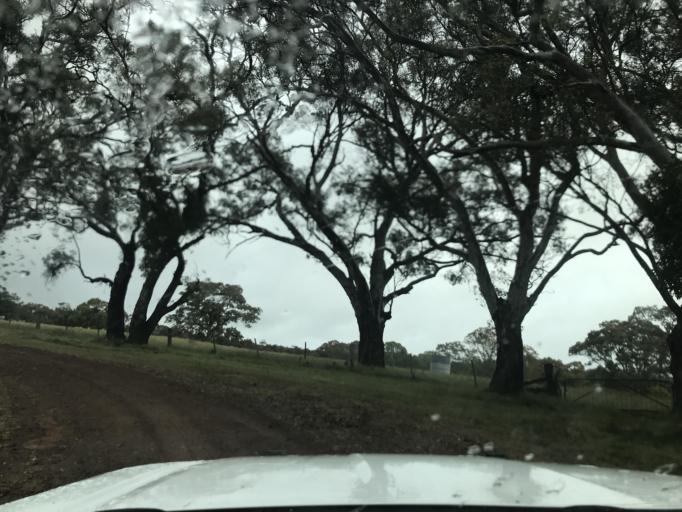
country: AU
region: South Australia
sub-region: Wattle Range
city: Penola
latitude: -37.2531
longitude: 141.3350
